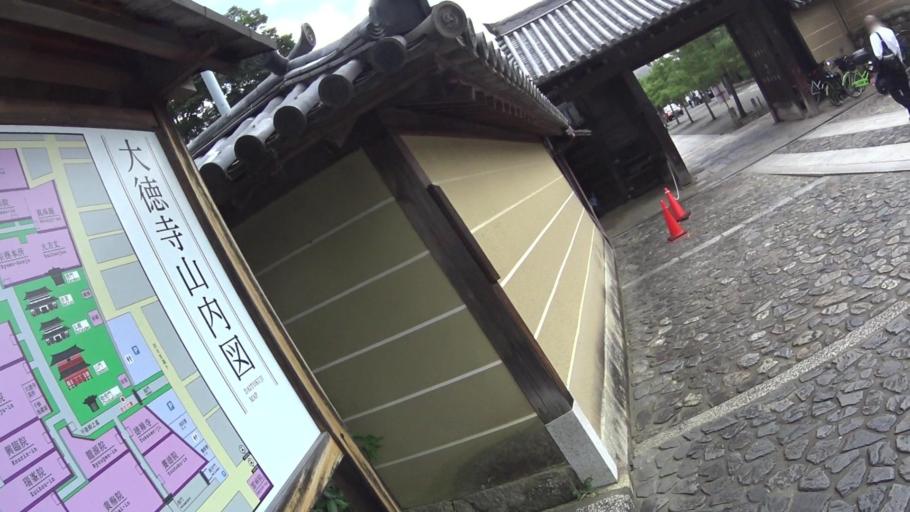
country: JP
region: Kyoto
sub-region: Kyoto-shi
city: Kamigyo-ku
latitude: 35.0444
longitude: 135.7460
